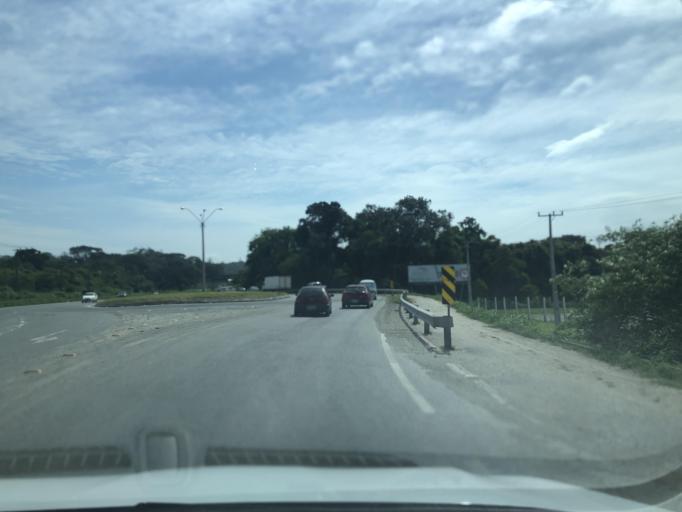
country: BR
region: Santa Catarina
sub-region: Sao Francisco Do Sul
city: Sao Francisco do Sul
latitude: -26.2506
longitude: -48.6096
